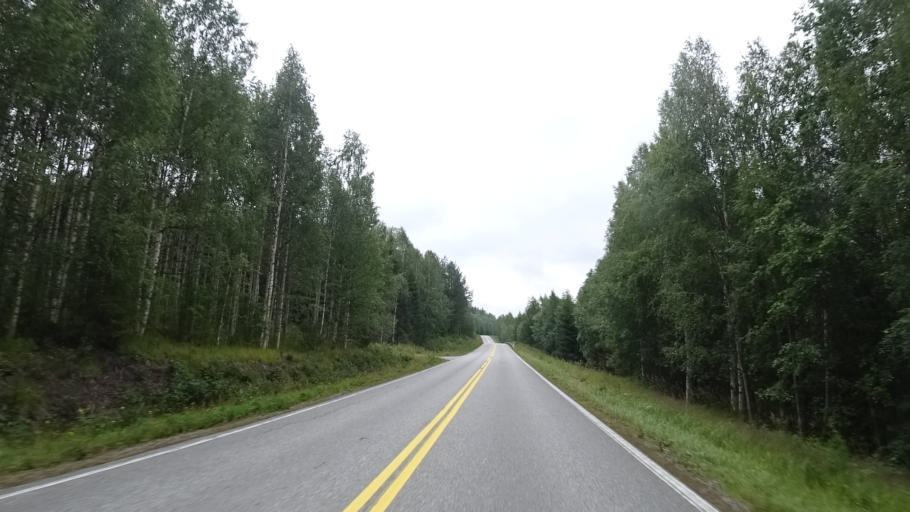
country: FI
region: North Karelia
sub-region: Pielisen Karjala
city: Lieksa
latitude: 63.2809
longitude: 30.5743
